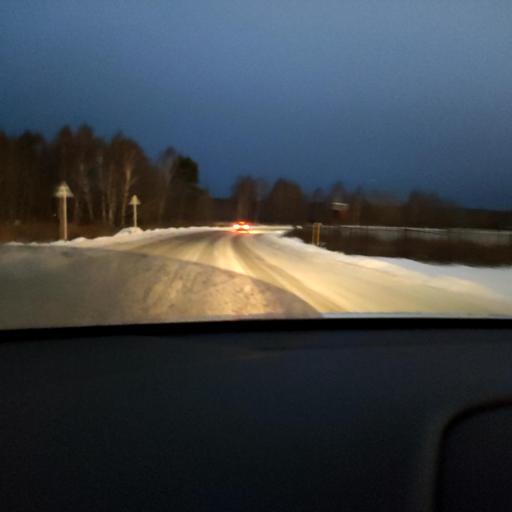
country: RU
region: Tatarstan
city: Osinovo
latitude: 55.8950
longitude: 48.8898
